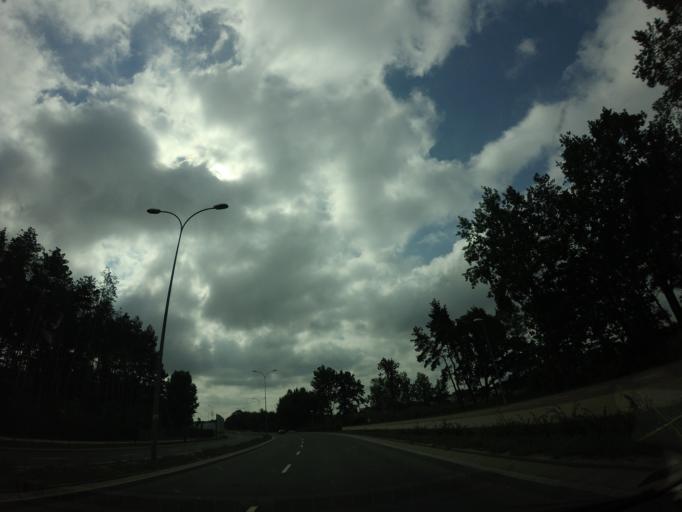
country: PL
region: Podlasie
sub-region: Bialystok
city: Bialystok
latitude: 53.1273
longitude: 23.2245
